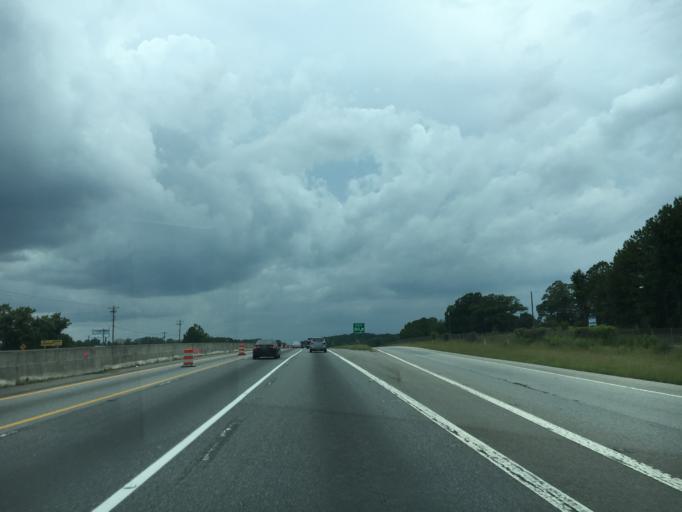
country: US
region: South Carolina
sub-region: Spartanburg County
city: Mayo
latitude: 35.0284
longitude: -81.8693
